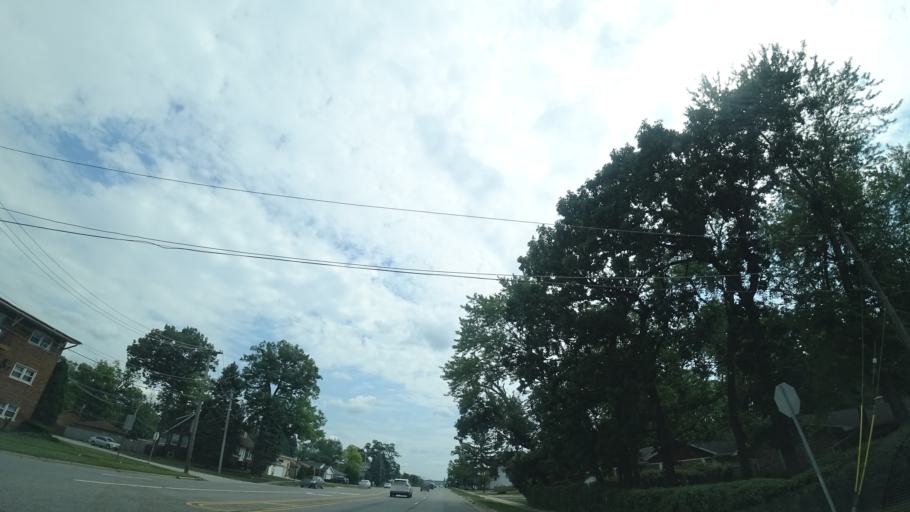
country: US
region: Illinois
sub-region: Cook County
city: Worth
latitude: 41.6941
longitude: -87.7977
